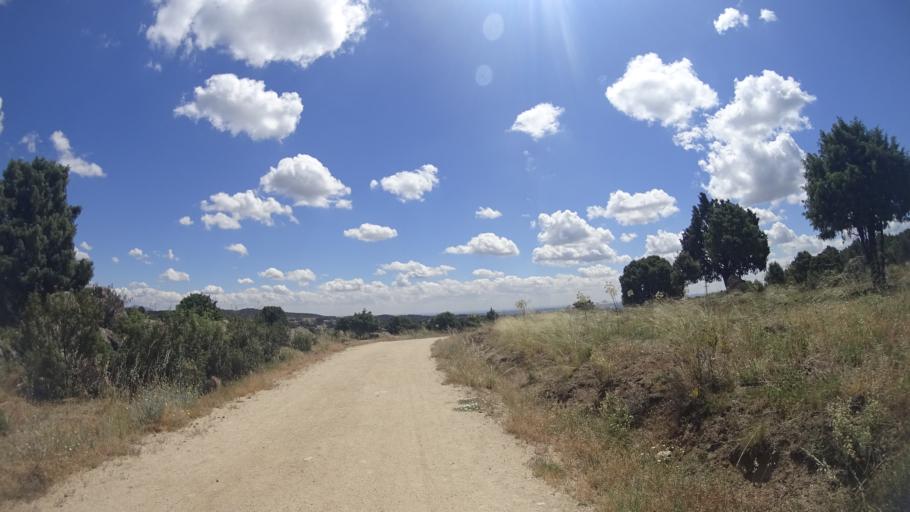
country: ES
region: Madrid
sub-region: Provincia de Madrid
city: Hoyo de Manzanares
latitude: 40.6023
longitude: -3.9166
